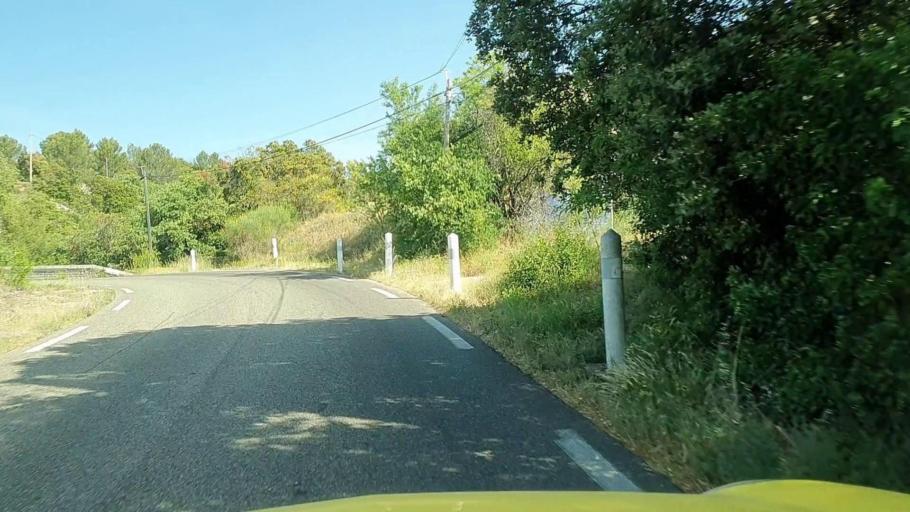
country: FR
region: Languedoc-Roussillon
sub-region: Departement du Gard
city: Montaren-et-Saint-Mediers
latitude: 44.0604
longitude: 4.3978
